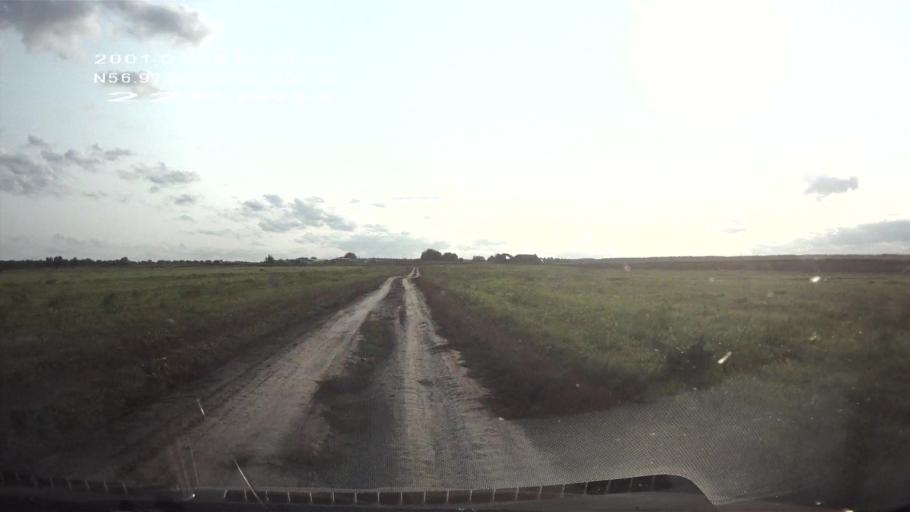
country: RU
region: Mariy-El
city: Kuzhener
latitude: 56.9737
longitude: 48.7946
